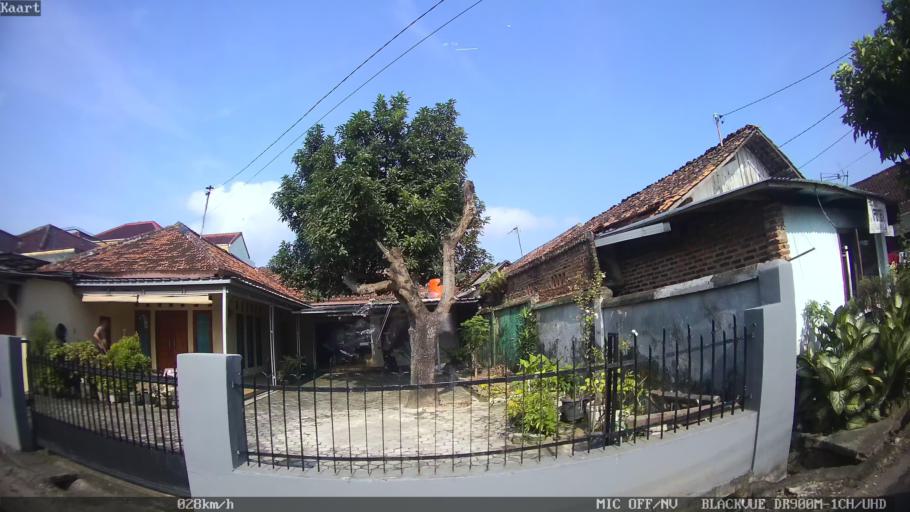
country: ID
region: Lampung
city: Kedaton
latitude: -5.3892
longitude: 105.2634
